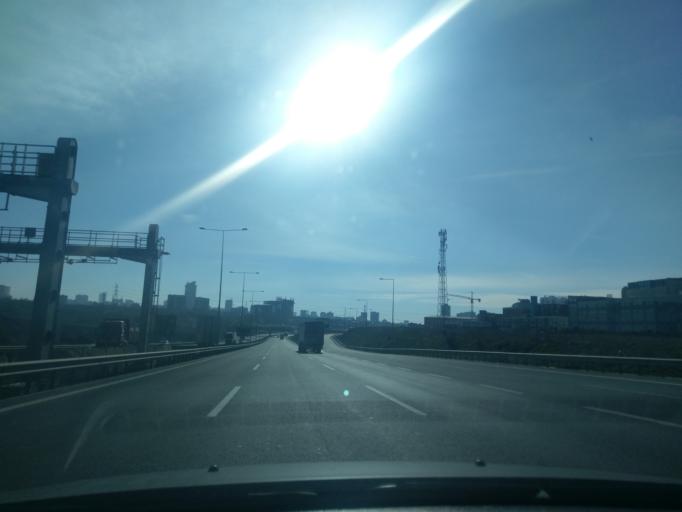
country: TR
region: Istanbul
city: Basaksehir
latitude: 41.0794
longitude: 28.8135
